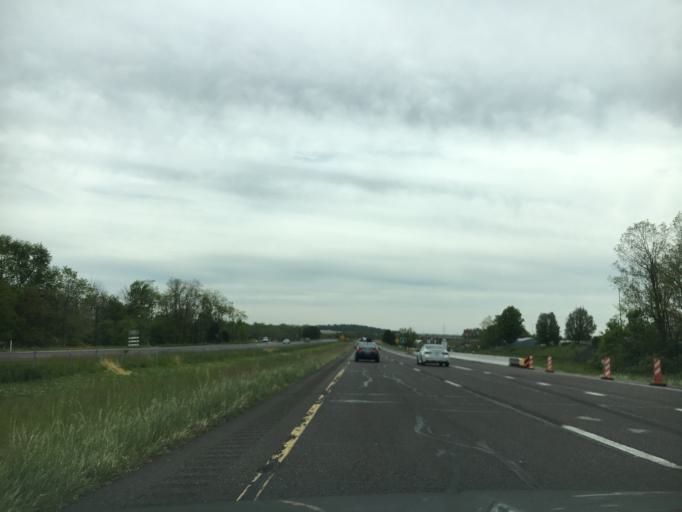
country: US
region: Pennsylvania
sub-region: Lancaster County
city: Ephrata
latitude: 40.1678
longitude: -76.1506
